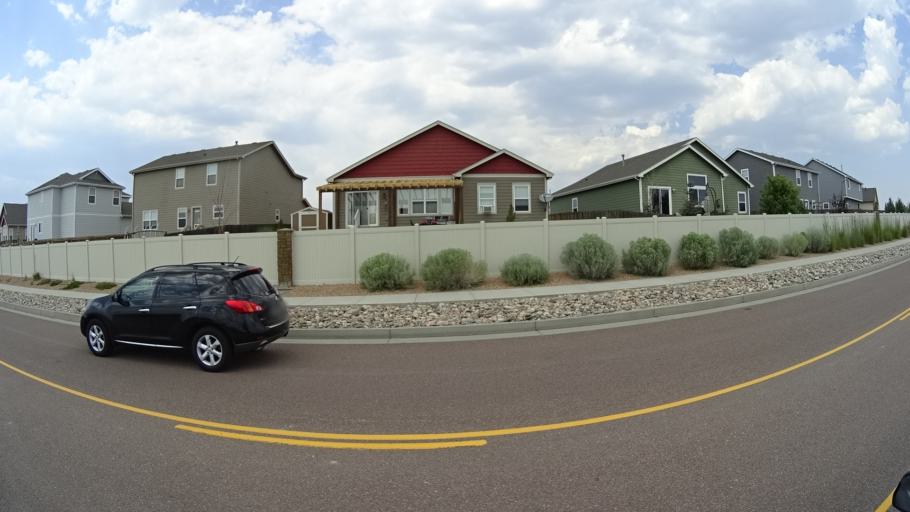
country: US
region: Colorado
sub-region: El Paso County
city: Black Forest
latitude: 38.9439
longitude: -104.6856
